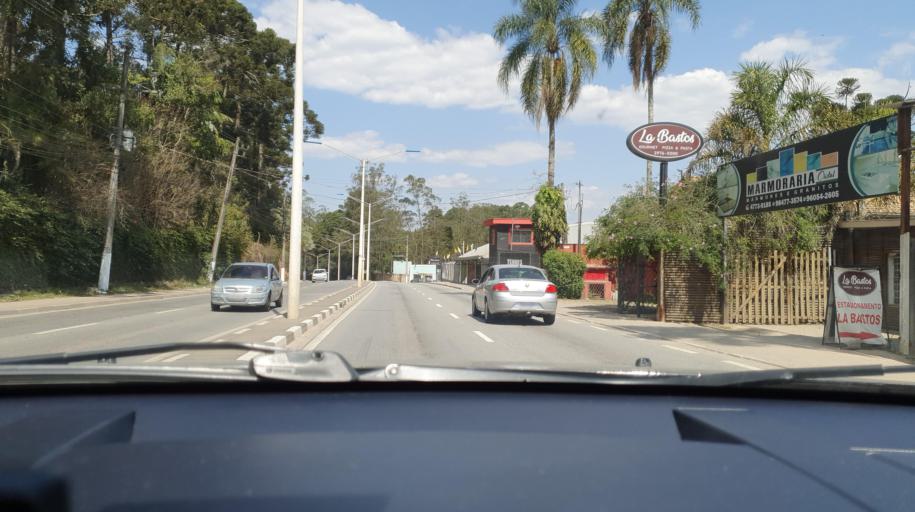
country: BR
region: Sao Paulo
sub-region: Vargem Grande Paulista
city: Vargem Grande Paulista
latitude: -23.6290
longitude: -46.9865
